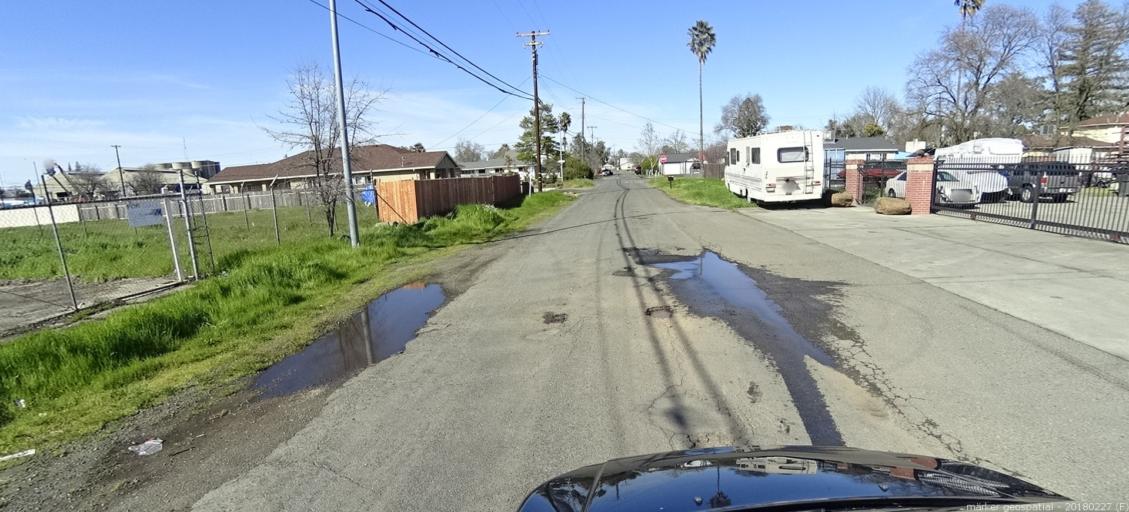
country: US
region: California
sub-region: Sacramento County
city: Rio Linda
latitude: 38.6922
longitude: -121.4489
